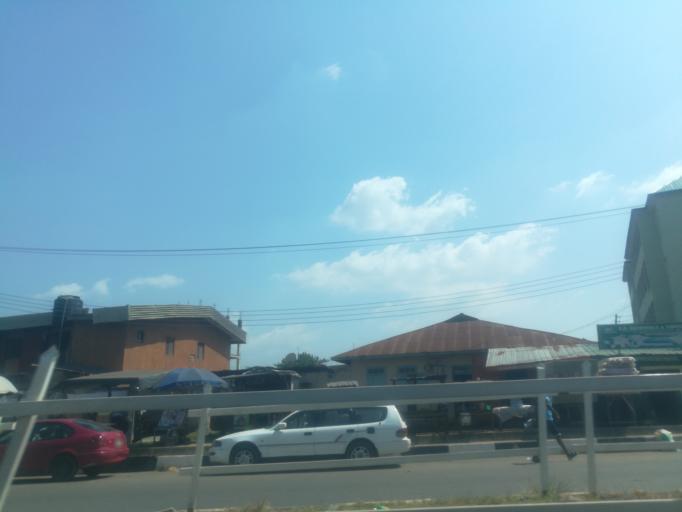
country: NG
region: Ogun
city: Abeokuta
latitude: 7.1407
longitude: 3.3376
